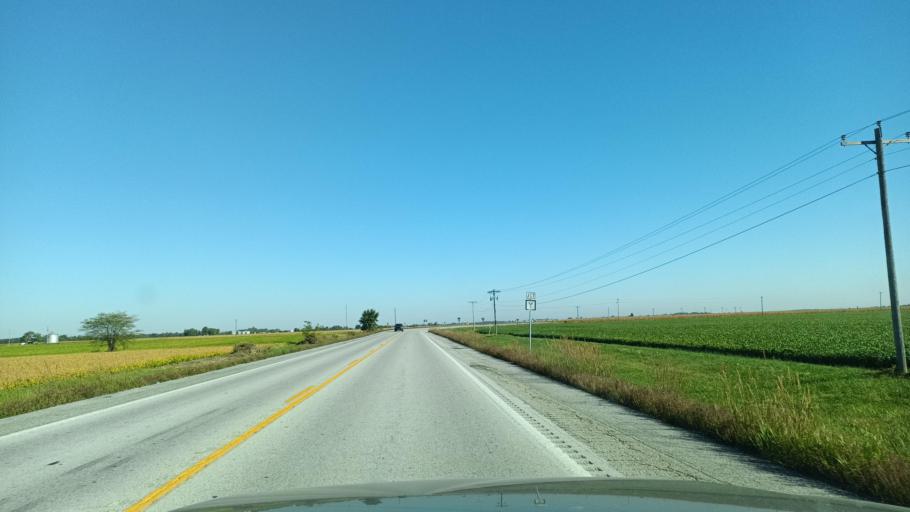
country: US
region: Missouri
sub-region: Audrain County
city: Vandalia
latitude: 39.4080
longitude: -91.6415
